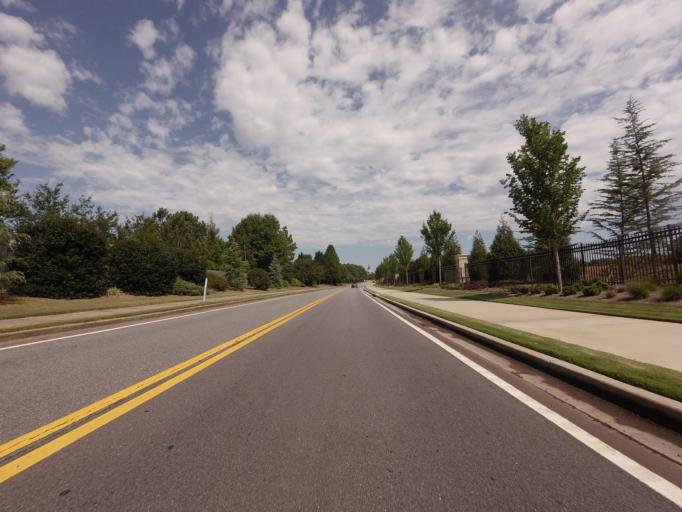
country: US
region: Georgia
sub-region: Fulton County
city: Johns Creek
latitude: 34.0448
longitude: -84.1673
